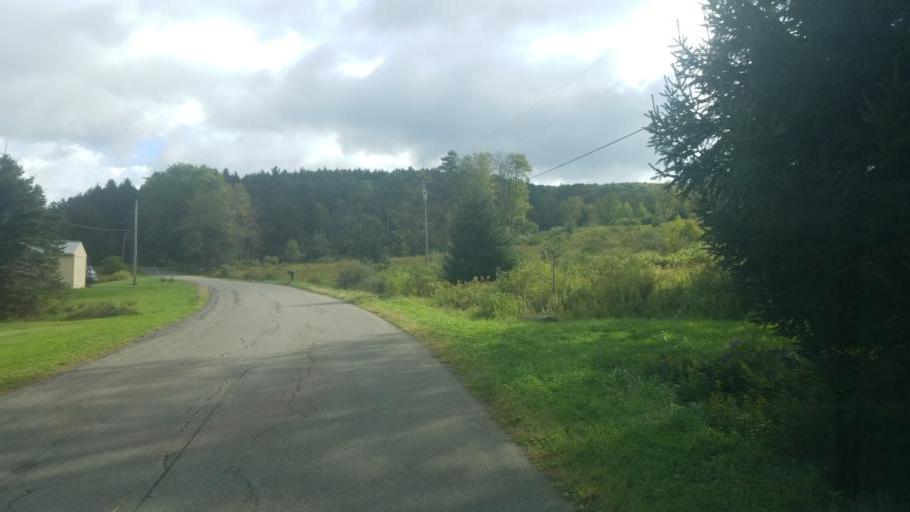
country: US
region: New York
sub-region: Cattaraugus County
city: Weston Mills
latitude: 42.1144
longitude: -78.3180
